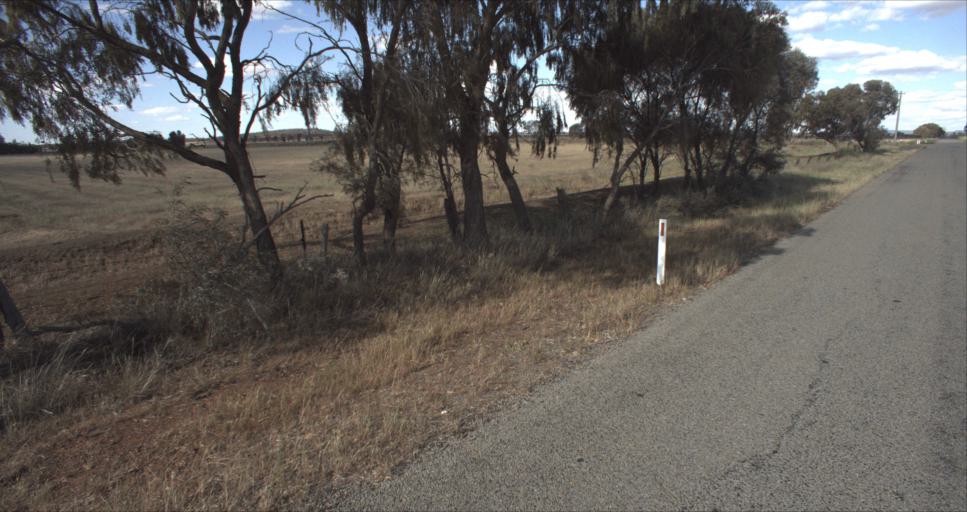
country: AU
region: New South Wales
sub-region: Leeton
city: Leeton
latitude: -34.4404
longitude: 146.2248
